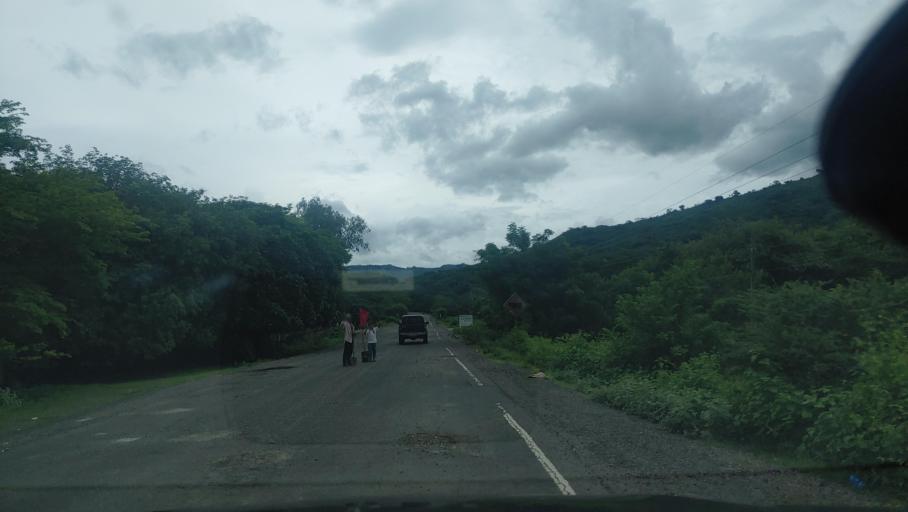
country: HN
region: Choluteca
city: Santa Ana de Yusguare
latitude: 13.3652
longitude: -87.0827
